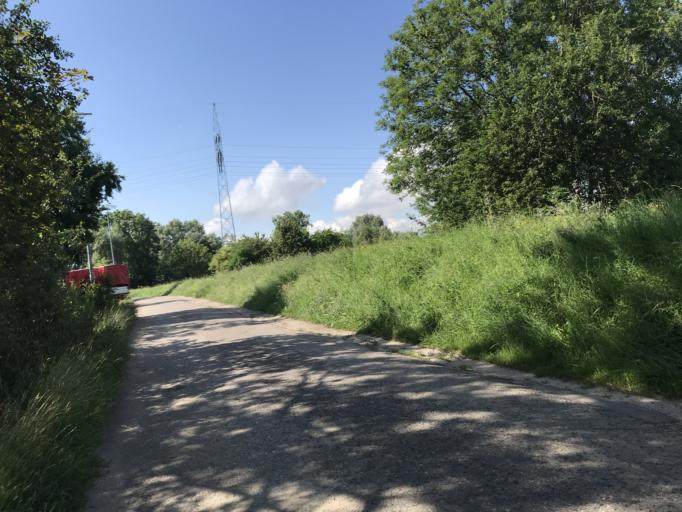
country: PL
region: Pomeranian Voivodeship
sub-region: Gdansk
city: Gdansk
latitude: 54.3299
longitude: 18.6568
